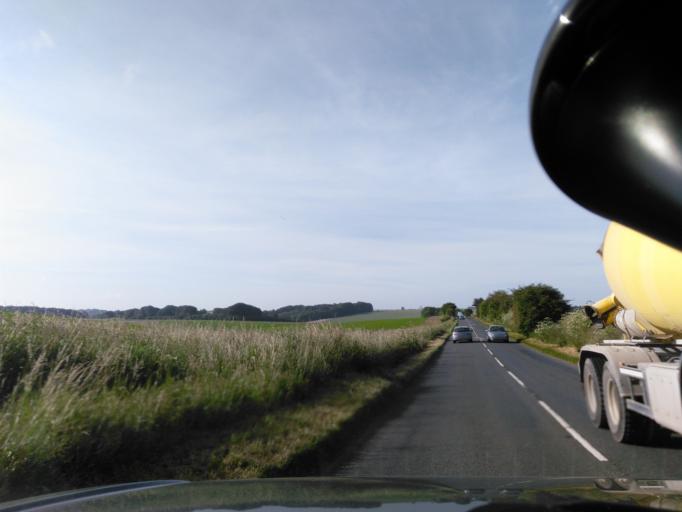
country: GB
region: England
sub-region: Wiltshire
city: Woodford
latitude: 51.1473
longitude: -1.8589
